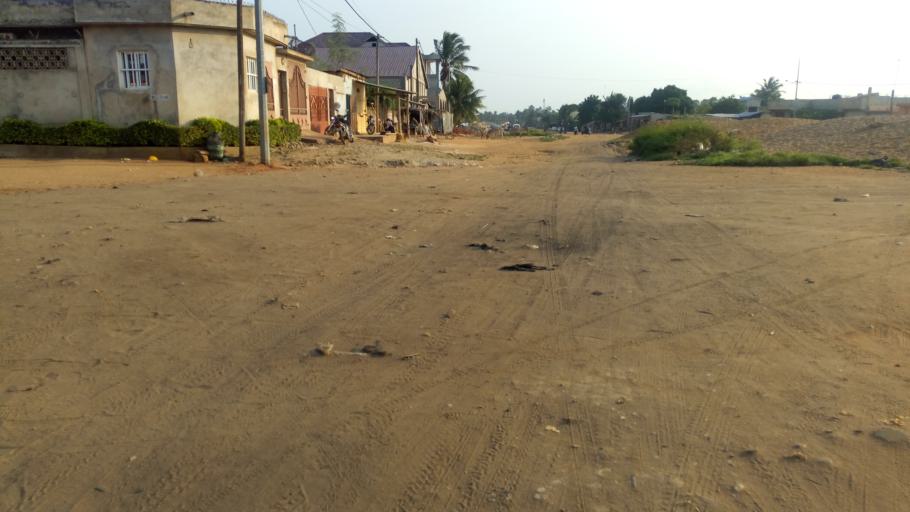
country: TG
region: Maritime
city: Lome
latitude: 6.1908
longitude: 1.1773
